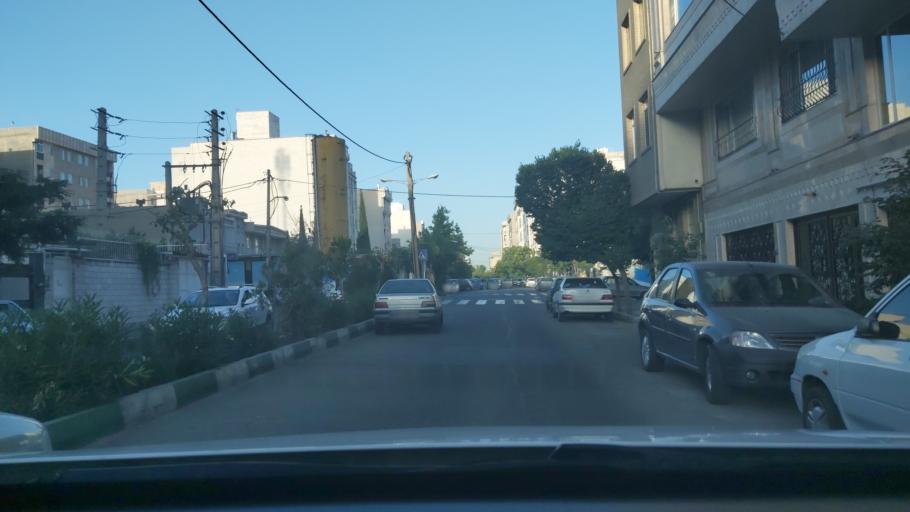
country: IR
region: Tehran
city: Tehran
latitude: 35.7312
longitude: 51.3068
